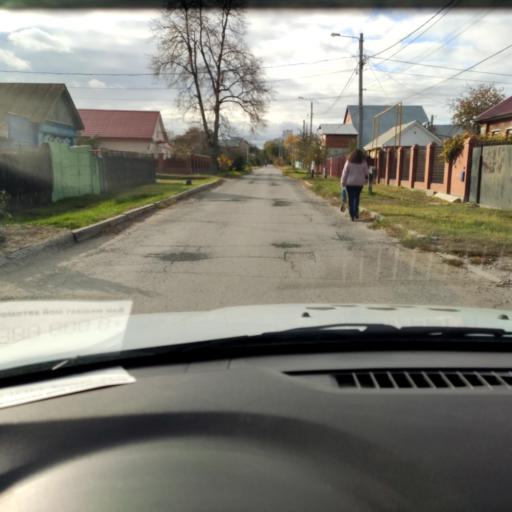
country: RU
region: Samara
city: Tol'yatti
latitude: 53.5267
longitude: 49.4269
